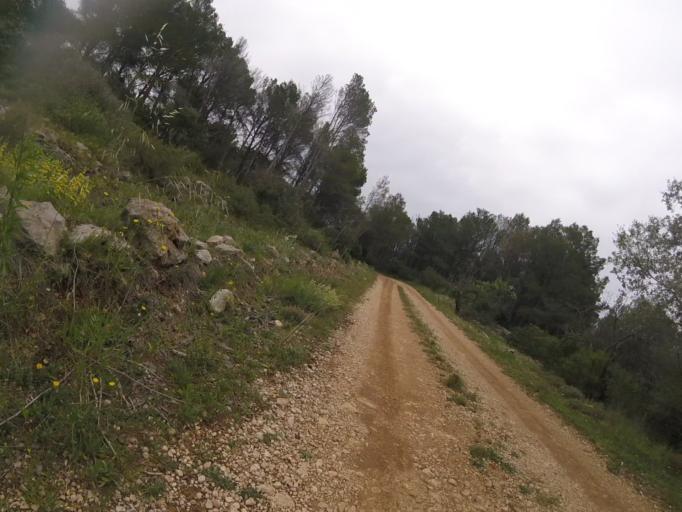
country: ES
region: Valencia
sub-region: Provincia de Castello
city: Alcala de Xivert
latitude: 40.3081
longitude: 0.2596
